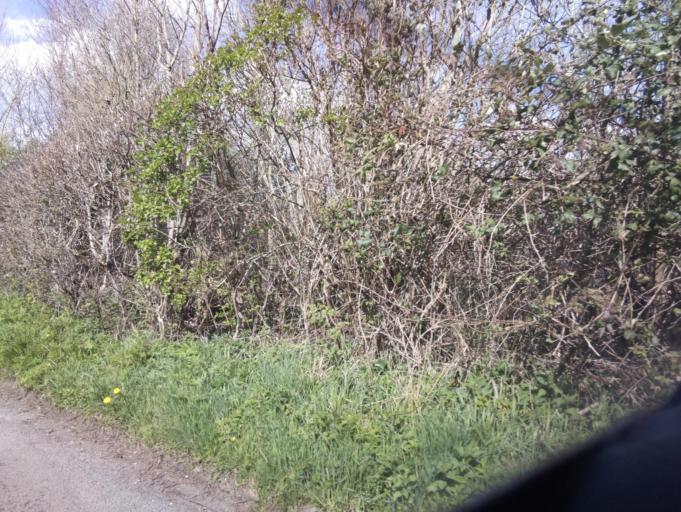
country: GB
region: England
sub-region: Hampshire
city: Andover
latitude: 51.1730
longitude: -1.4848
